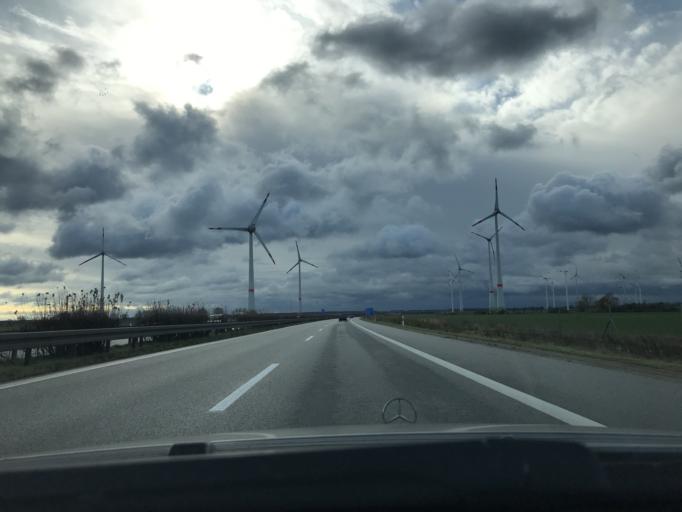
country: DE
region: Mecklenburg-Vorpommern
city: Kessin
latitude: 53.7216
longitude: 13.3334
